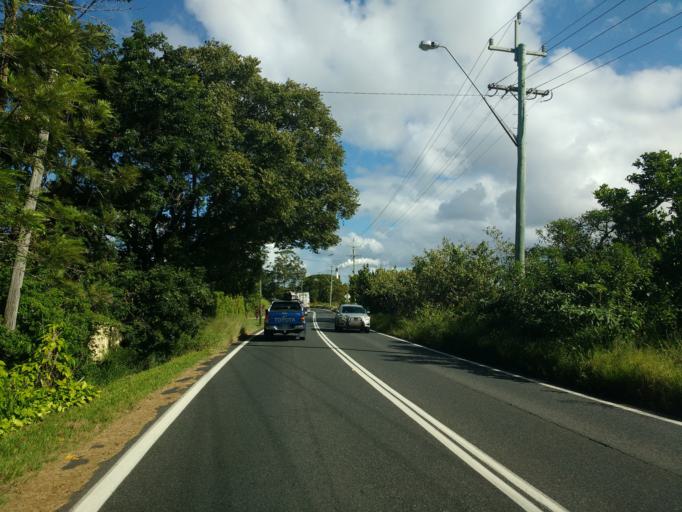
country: AU
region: New South Wales
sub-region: Richmond Valley
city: Evans Head
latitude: -29.0040
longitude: 153.4365
